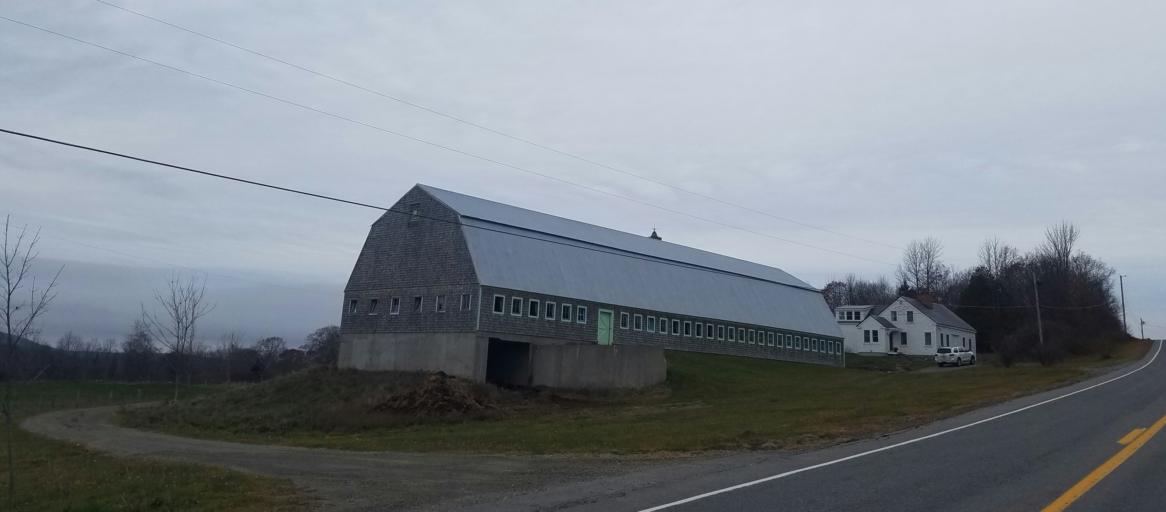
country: US
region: Maine
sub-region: Waldo County
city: Brooks
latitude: 44.5092
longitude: -69.1052
